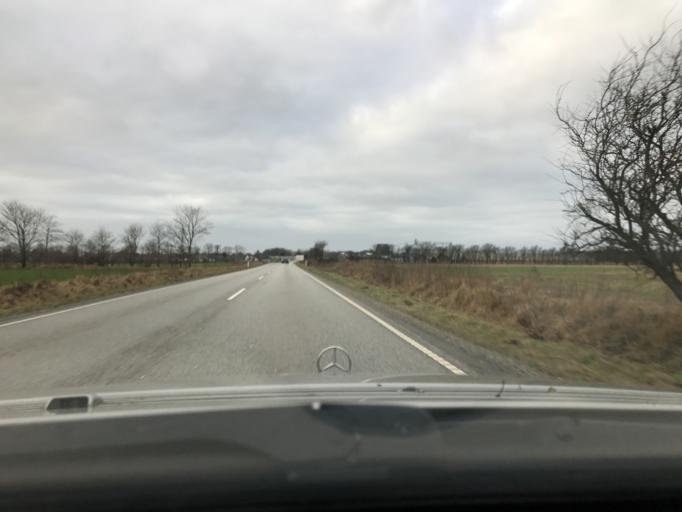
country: DK
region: South Denmark
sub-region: Aabenraa Kommune
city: Rodekro
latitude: 55.0764
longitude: 9.2294
